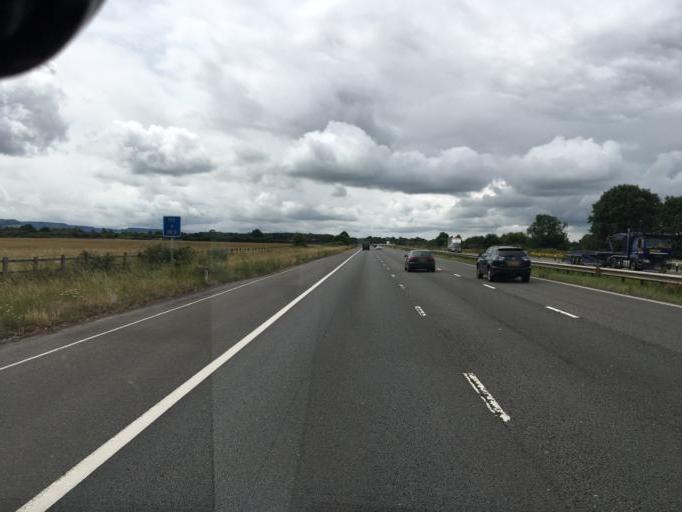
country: GB
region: England
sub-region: Gloucestershire
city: Stonehouse
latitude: 51.7866
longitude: -2.3008
